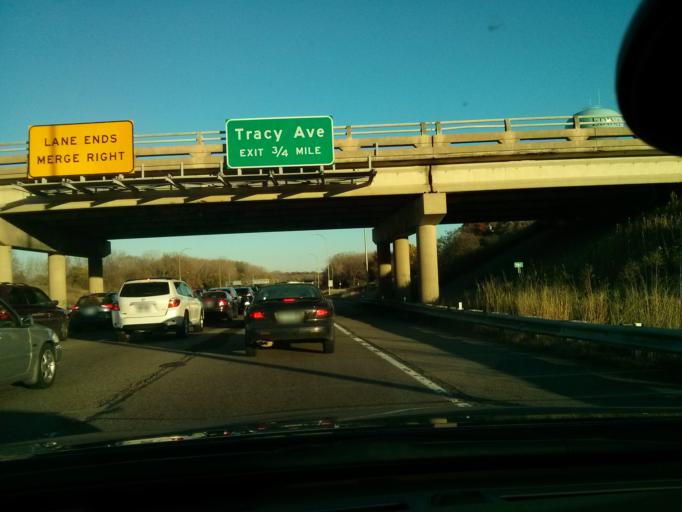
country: US
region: Minnesota
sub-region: Hennepin County
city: Edina
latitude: 44.8895
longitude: -93.3874
